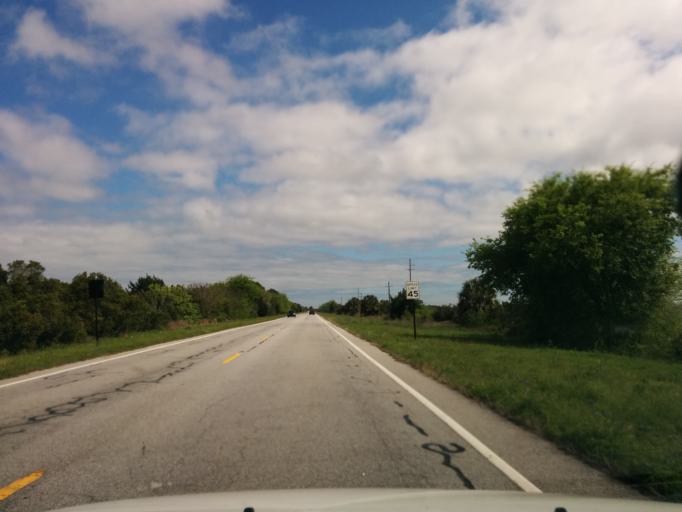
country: US
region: Georgia
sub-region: Glynn County
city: Brunswick
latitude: 31.0650
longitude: -81.4552
